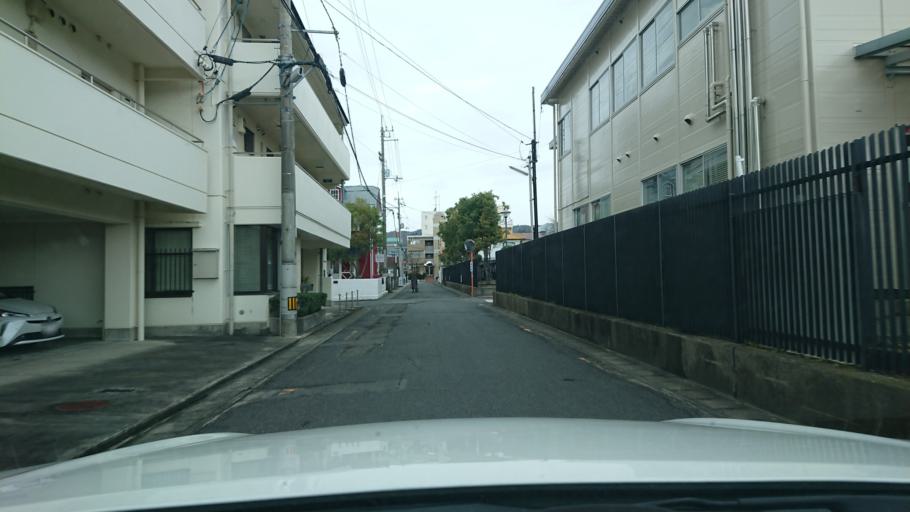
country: JP
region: Tokushima
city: Tokushima-shi
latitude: 34.0519
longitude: 134.5579
